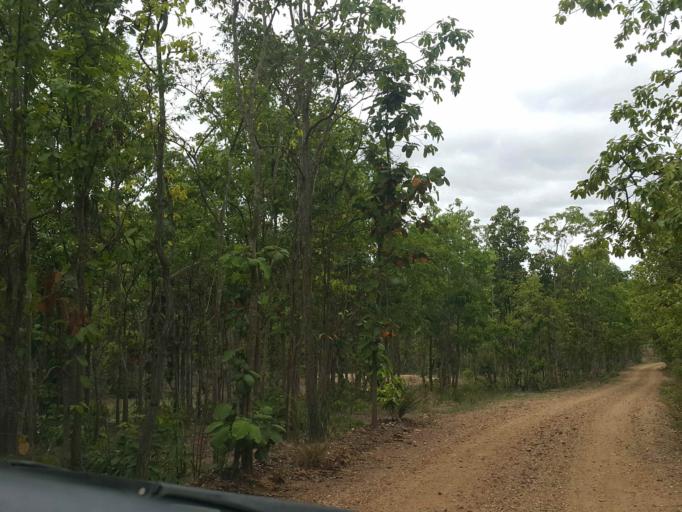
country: TH
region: Chiang Mai
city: Doi Lo
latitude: 18.5039
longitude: 98.7506
